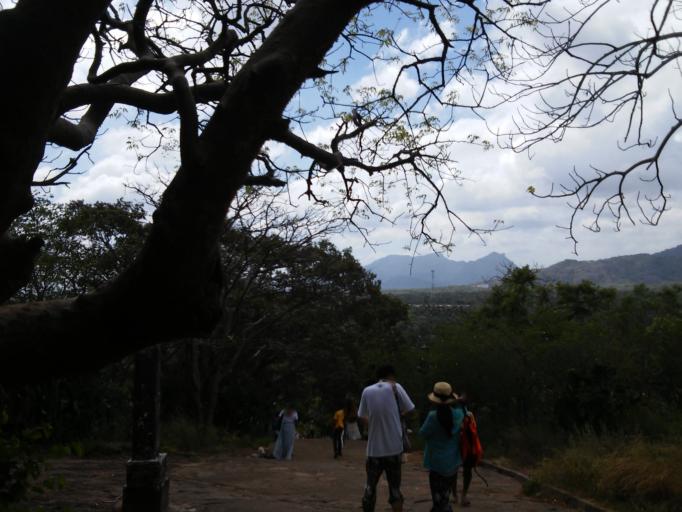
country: LK
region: Central
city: Dambulla
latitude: 7.8548
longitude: 80.6504
